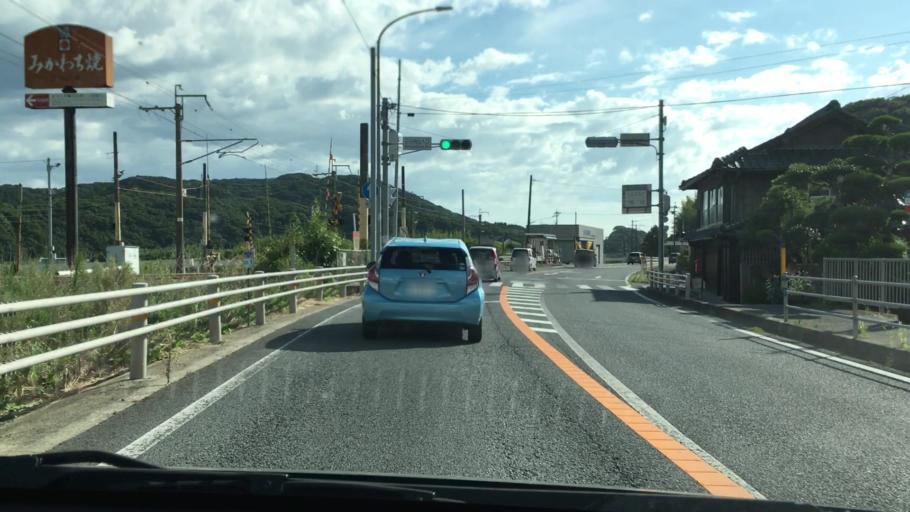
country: JP
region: Nagasaki
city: Sasebo
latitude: 33.1461
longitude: 129.8273
